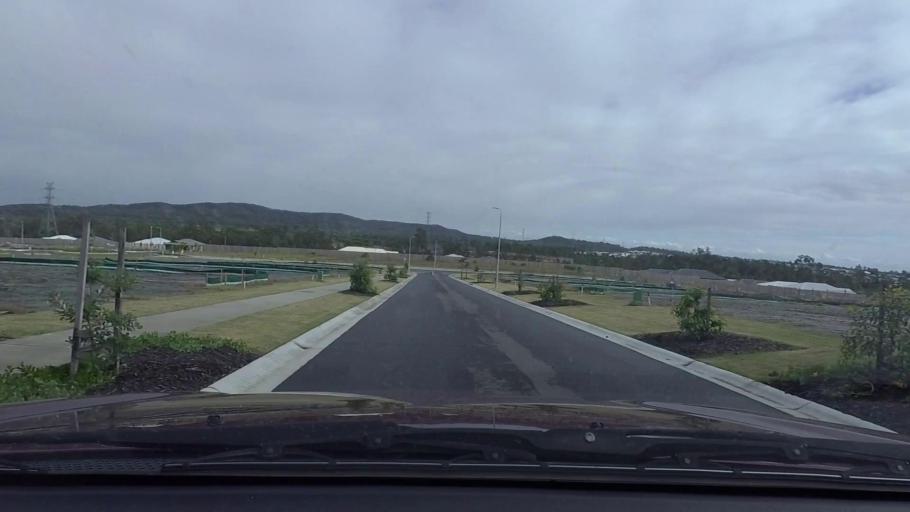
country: AU
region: Queensland
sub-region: Logan
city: Chambers Flat
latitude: -27.8163
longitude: 153.1318
